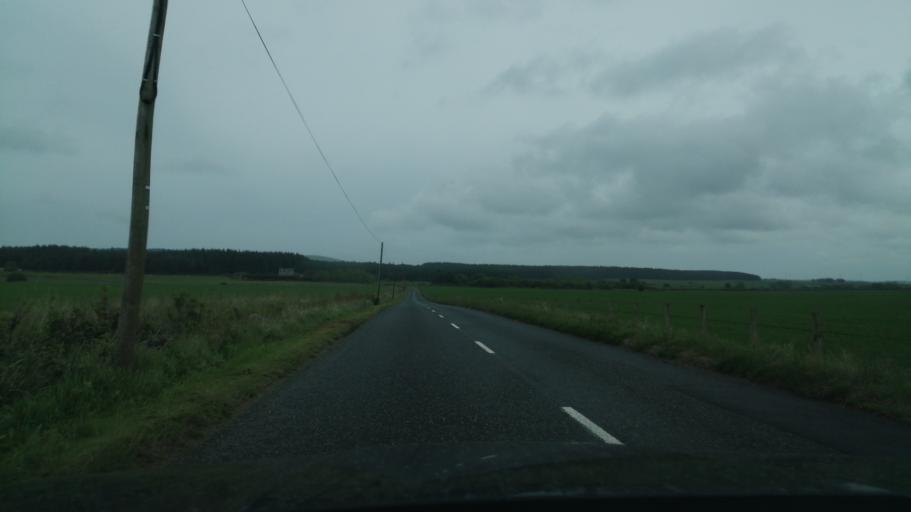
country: GB
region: Scotland
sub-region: Aberdeenshire
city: Portsoy
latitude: 57.6143
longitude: -2.7232
